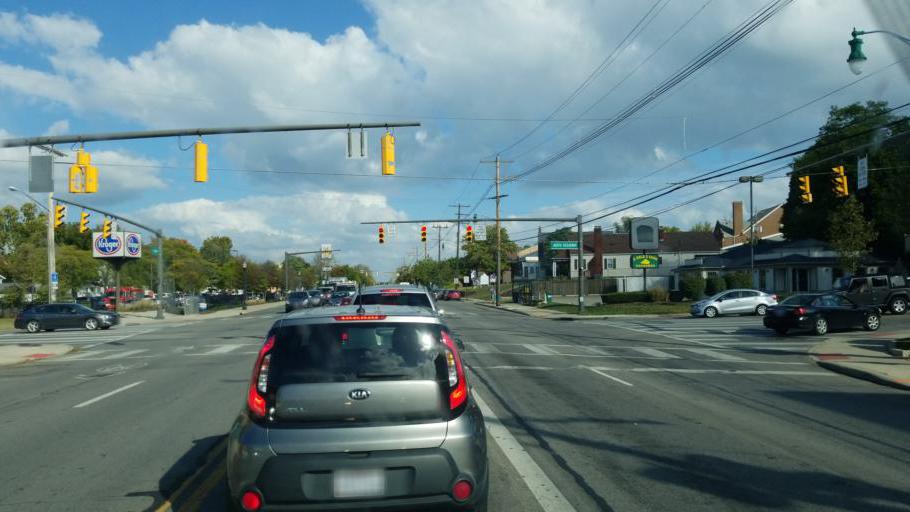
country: US
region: Ohio
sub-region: Franklin County
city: Grandview Heights
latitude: 40.0313
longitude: -83.0158
